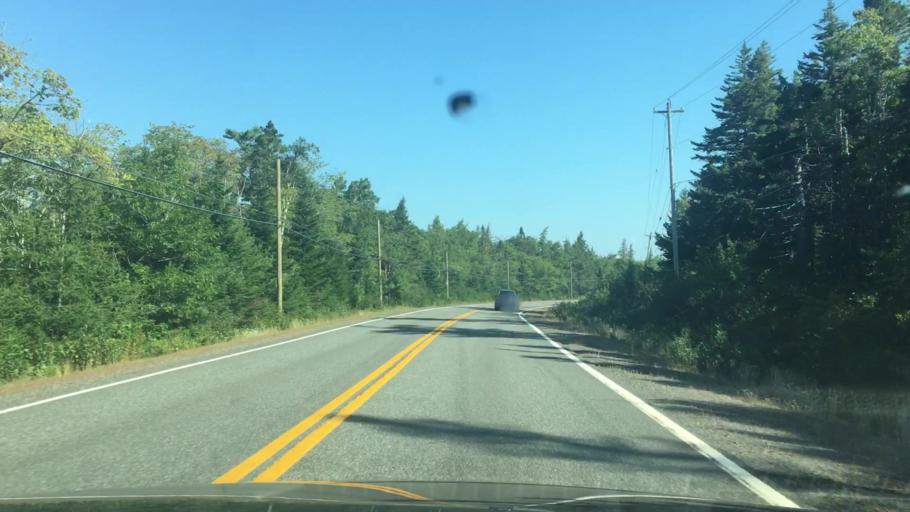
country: CA
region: Nova Scotia
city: Cole Harbour
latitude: 44.7951
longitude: -62.8887
